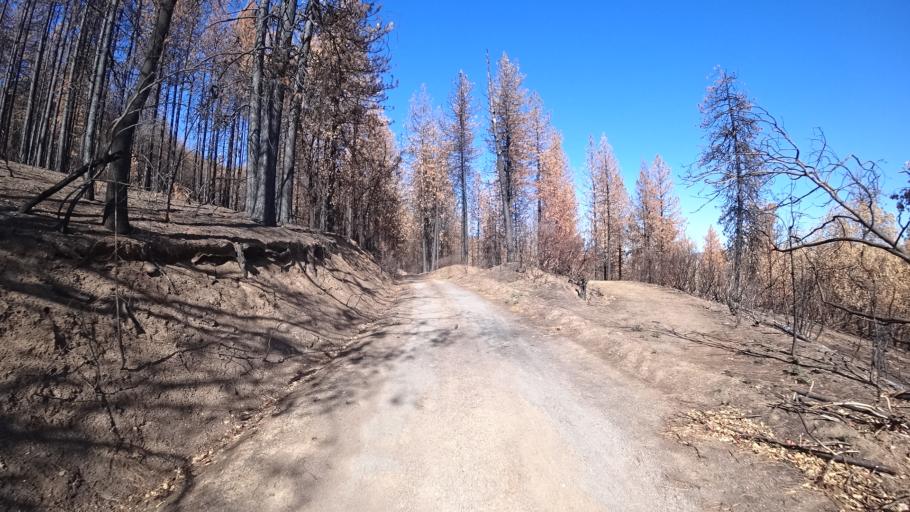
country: US
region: California
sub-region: Tehama County
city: Rancho Tehama Reserve
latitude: 39.6719
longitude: -122.6944
